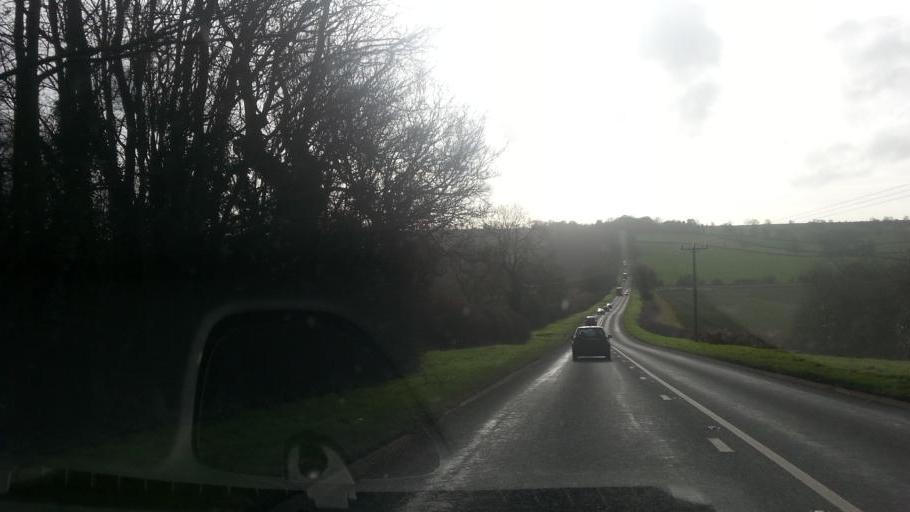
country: GB
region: England
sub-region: District of Rutland
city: Manton
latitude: 52.6282
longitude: -0.7089
